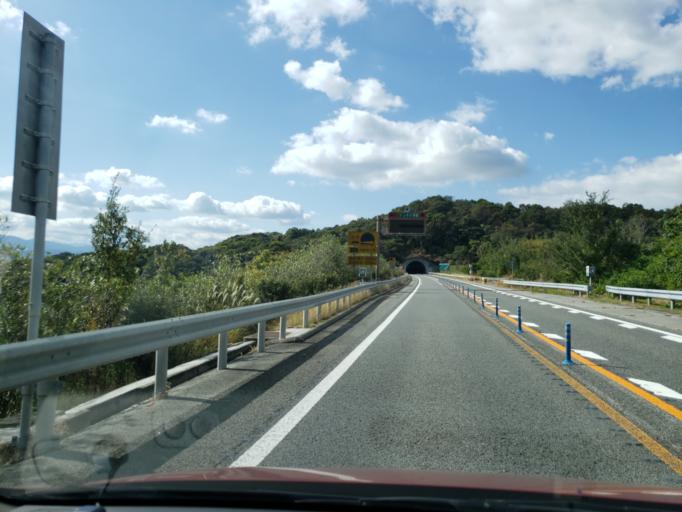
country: JP
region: Tokushima
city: Kamojimacho-jogejima
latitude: 34.1164
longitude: 134.3260
